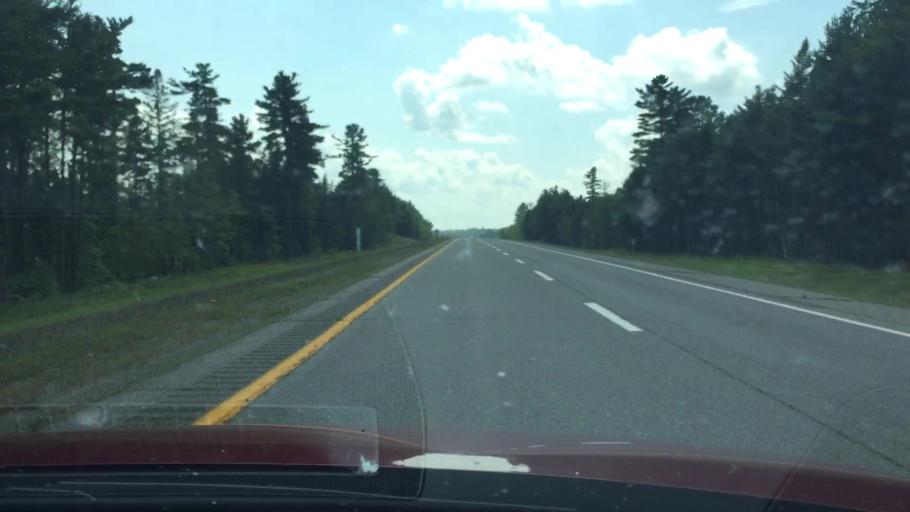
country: US
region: Maine
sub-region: Penobscot County
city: Medway
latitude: 45.4824
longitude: -68.5725
